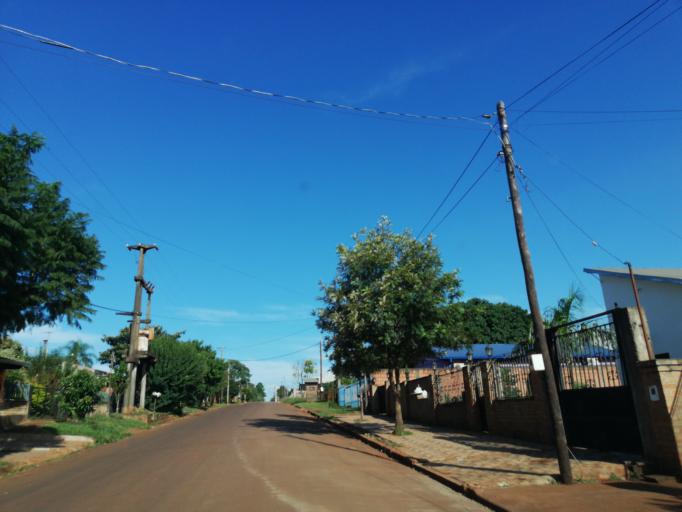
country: AR
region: Misiones
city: Dos de Mayo
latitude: -26.9940
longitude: -54.4944
